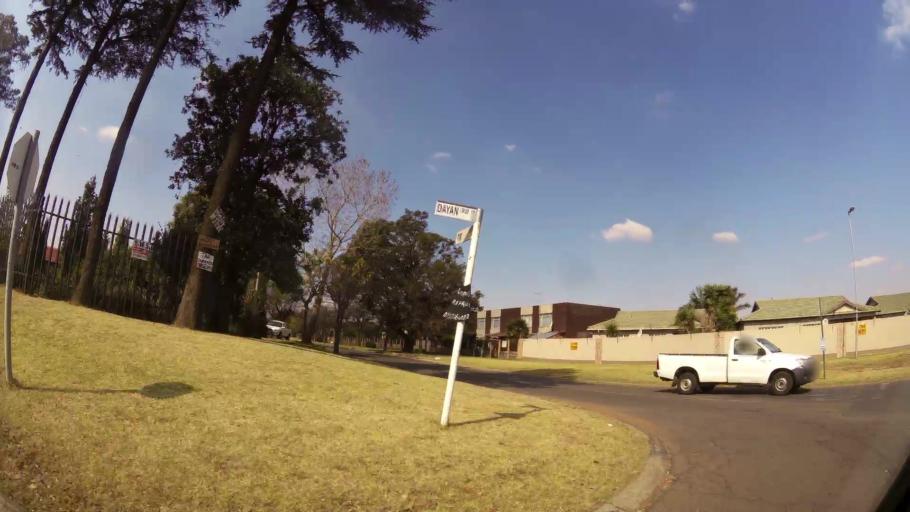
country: ZA
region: Gauteng
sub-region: Ekurhuleni Metropolitan Municipality
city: Boksburg
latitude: -26.1879
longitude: 28.2328
